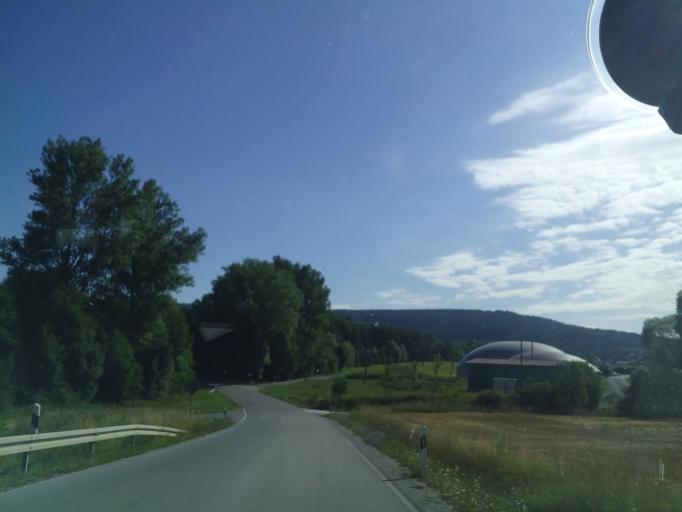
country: DE
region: Bavaria
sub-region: Upper Franconia
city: Buttenheim
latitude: 49.8070
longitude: 11.0637
